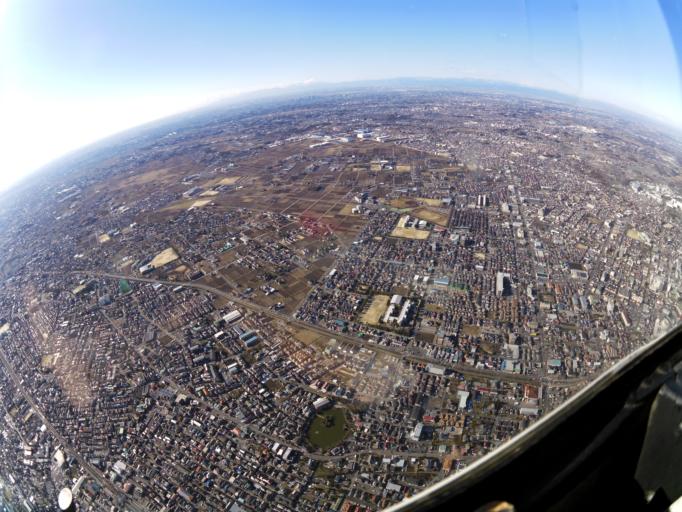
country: JP
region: Saitama
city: Kasukabe
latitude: 35.9686
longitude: 139.7644
